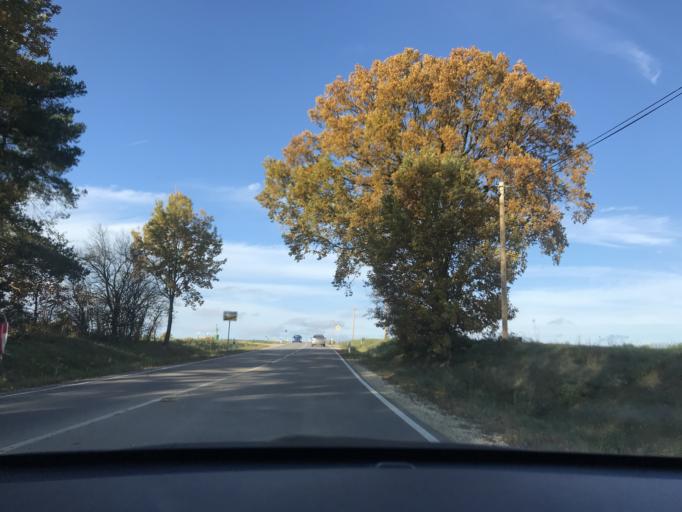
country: DE
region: Bavaria
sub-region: Lower Bavaria
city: Bad Abbach
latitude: 48.9424
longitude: 12.0849
